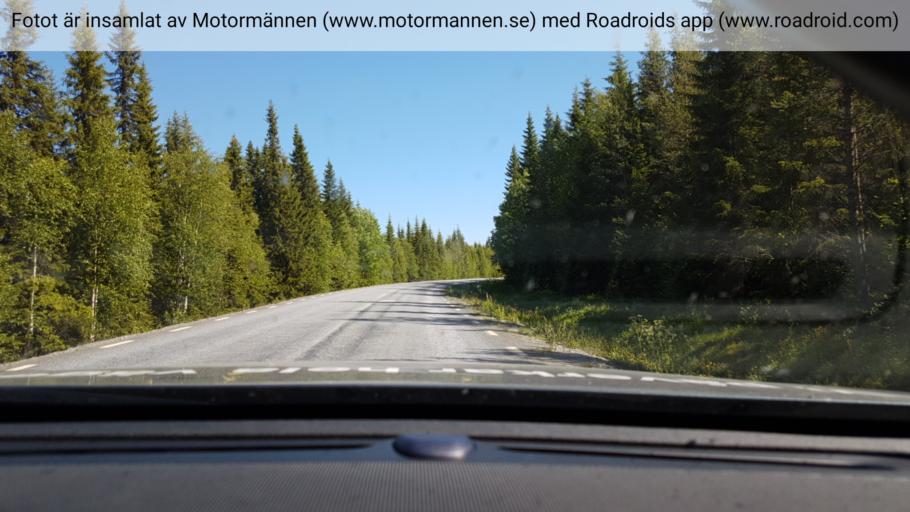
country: SE
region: Vaesterbotten
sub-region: Vilhelmina Kommun
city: Sjoberg
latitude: 64.7411
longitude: 16.2039
